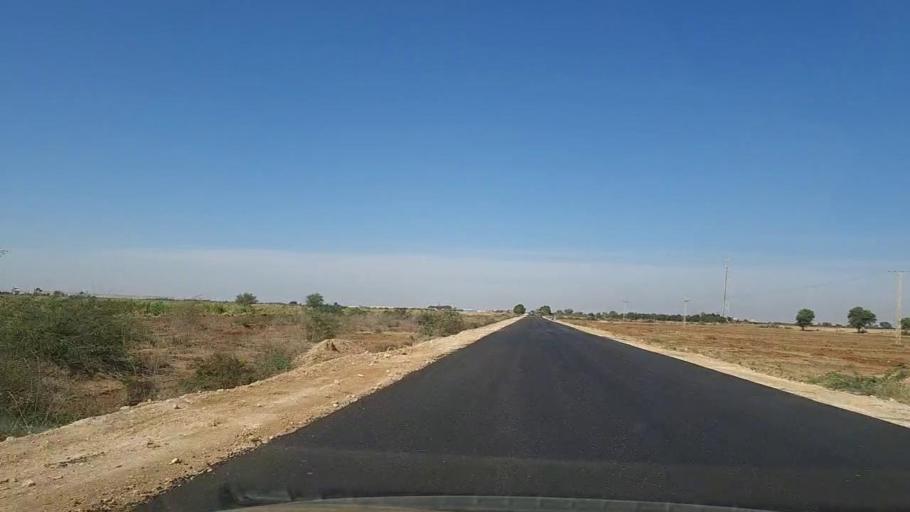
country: PK
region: Sindh
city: Kotri
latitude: 25.2449
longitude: 68.2296
